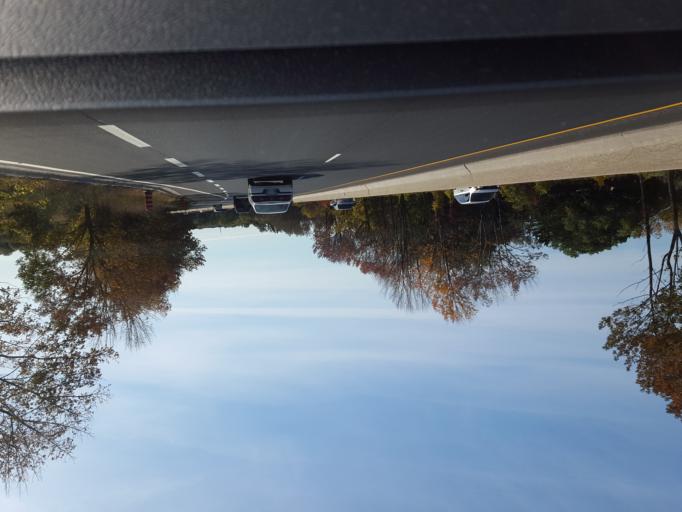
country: CA
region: Ontario
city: Oshawa
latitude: 43.9321
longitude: -78.5991
